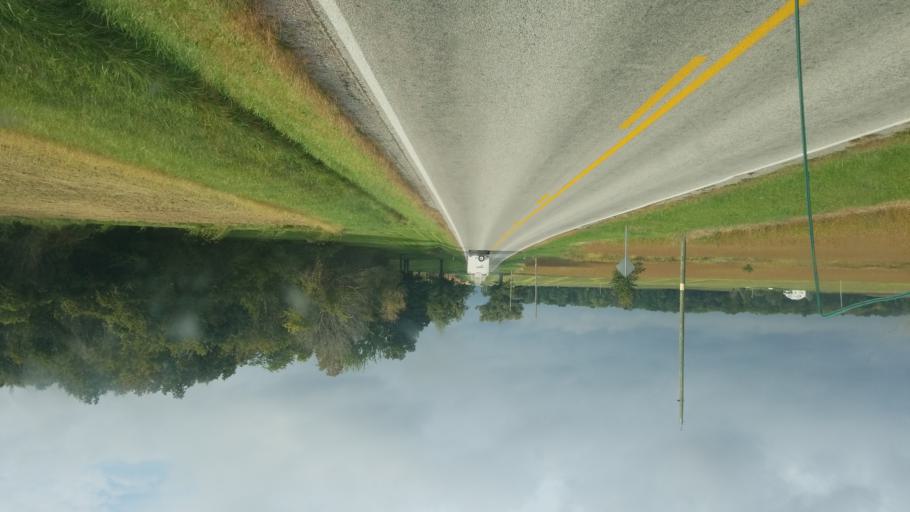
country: US
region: Ohio
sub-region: Seneca County
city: Fostoria
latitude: 41.0484
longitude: -83.4770
